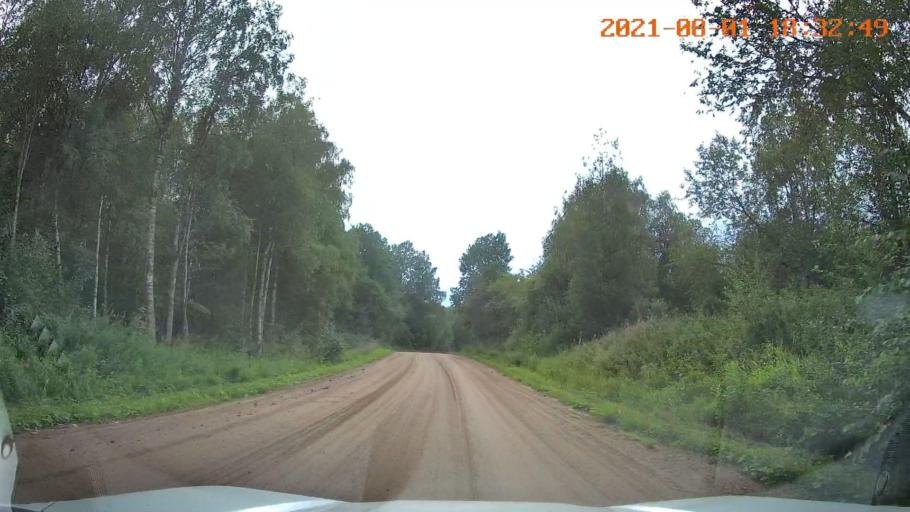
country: RU
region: Leningrad
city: Voznesen'ye
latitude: 60.8922
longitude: 35.3187
